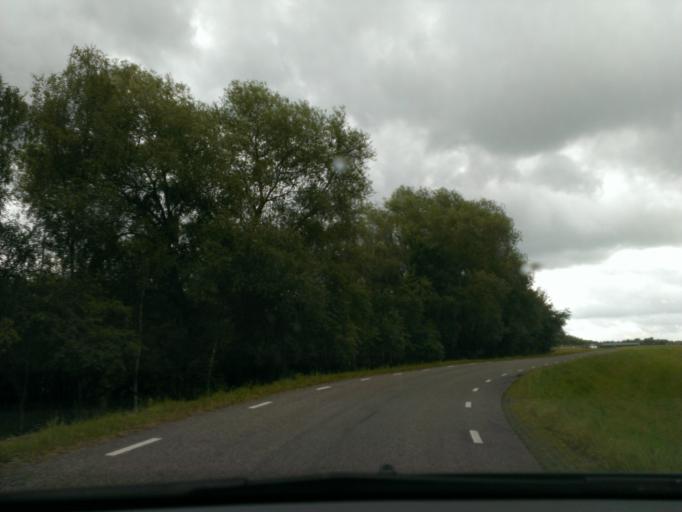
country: NL
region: Overijssel
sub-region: Gemeente Olst-Wijhe
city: Olst
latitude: 52.2993
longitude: 6.0941
